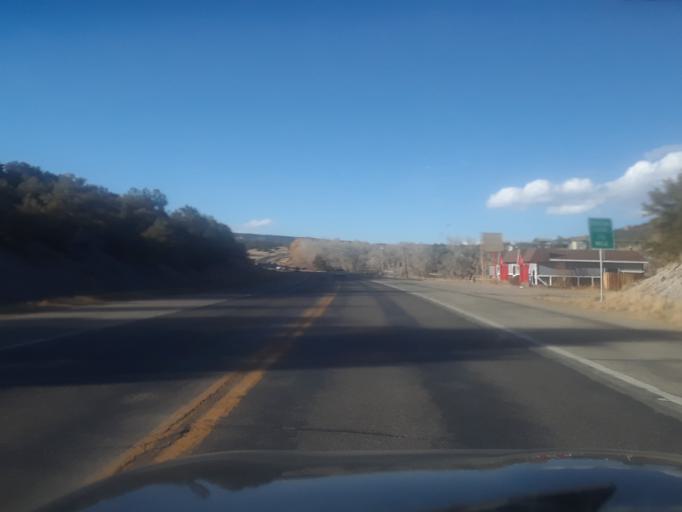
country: US
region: Colorado
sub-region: Chaffee County
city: Salida
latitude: 38.6302
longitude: -106.0786
